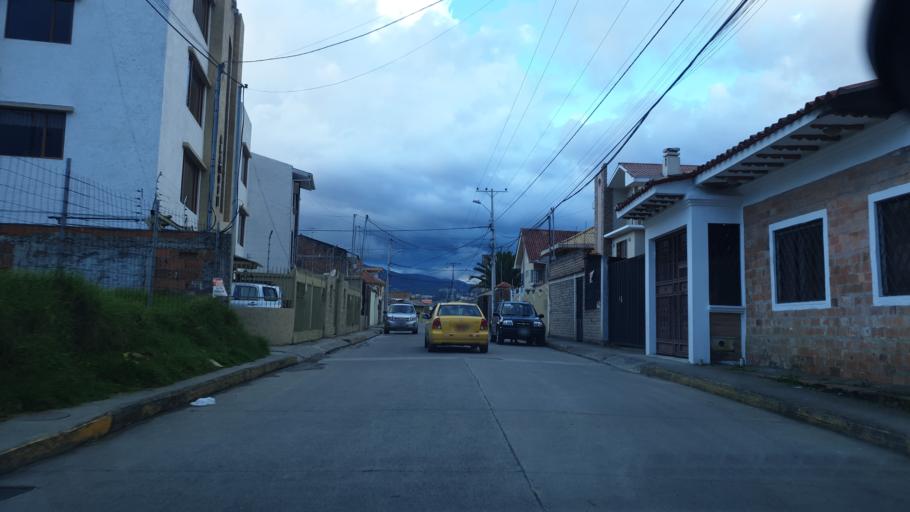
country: EC
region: Azuay
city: Cuenca
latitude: -2.9180
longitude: -79.0284
